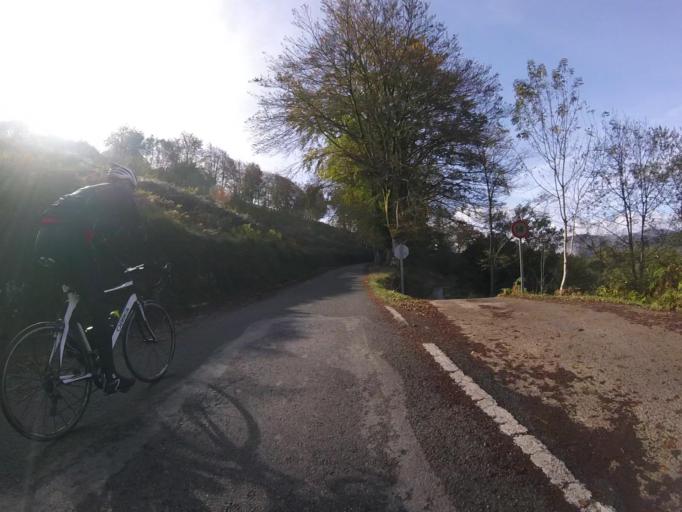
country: ES
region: Navarre
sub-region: Provincia de Navarra
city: Arano
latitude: 43.2051
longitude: -1.8955
